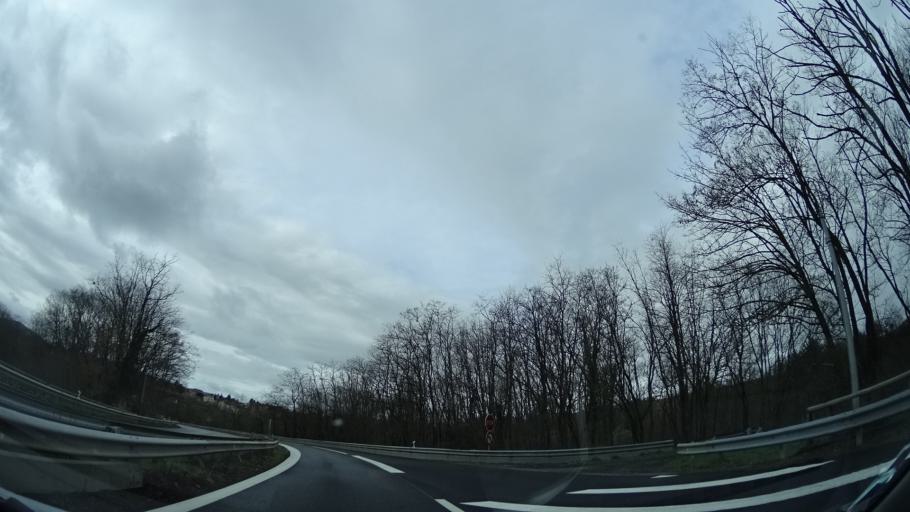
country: FR
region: Rhone-Alpes
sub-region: Departement du Rhone
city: Saint-Germain-Nuelles
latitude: 45.8391
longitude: 4.6271
